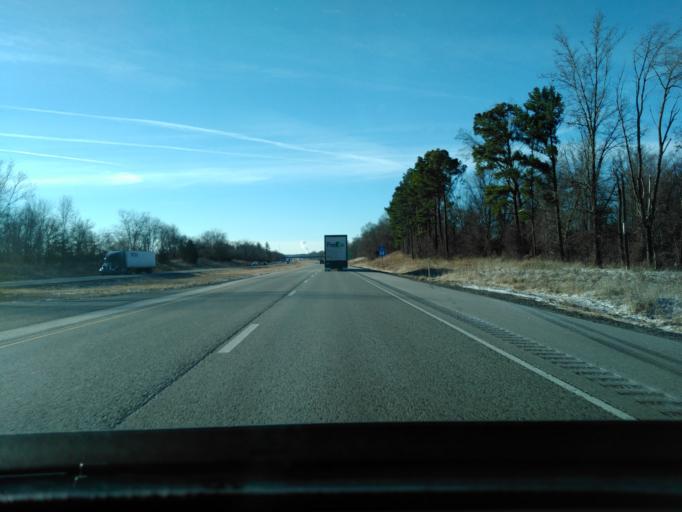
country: US
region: Illinois
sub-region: Williamson County
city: Johnston City
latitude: 37.8251
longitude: -88.9458
